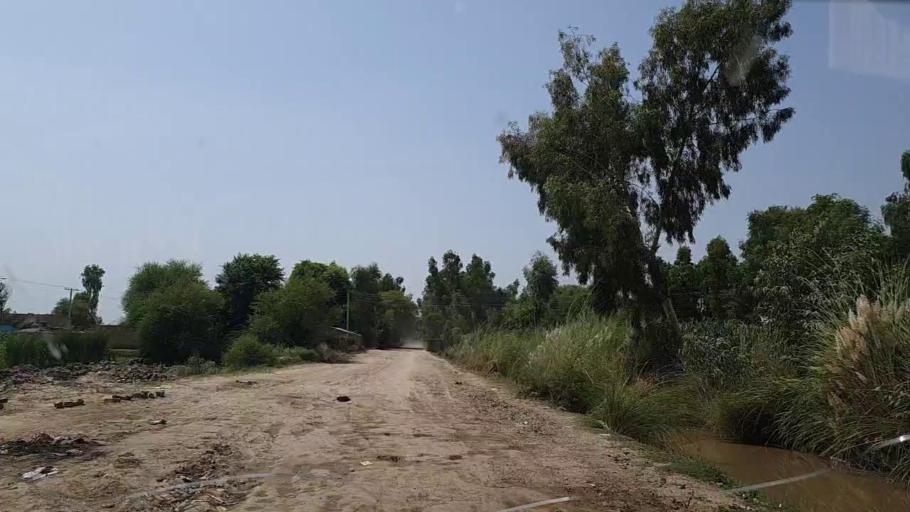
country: PK
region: Sindh
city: Ghotki
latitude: 28.0887
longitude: 69.3350
